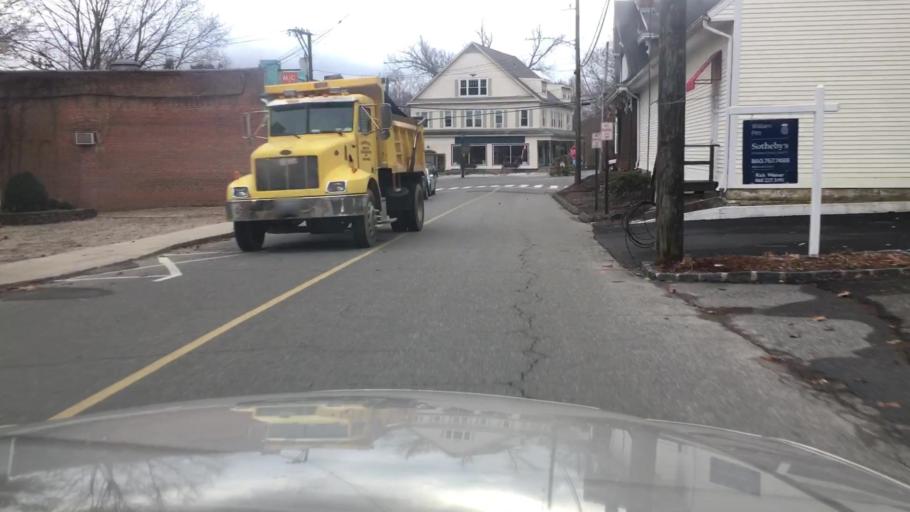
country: US
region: Connecticut
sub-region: Middlesex County
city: Essex Village
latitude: 41.3540
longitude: -72.3909
